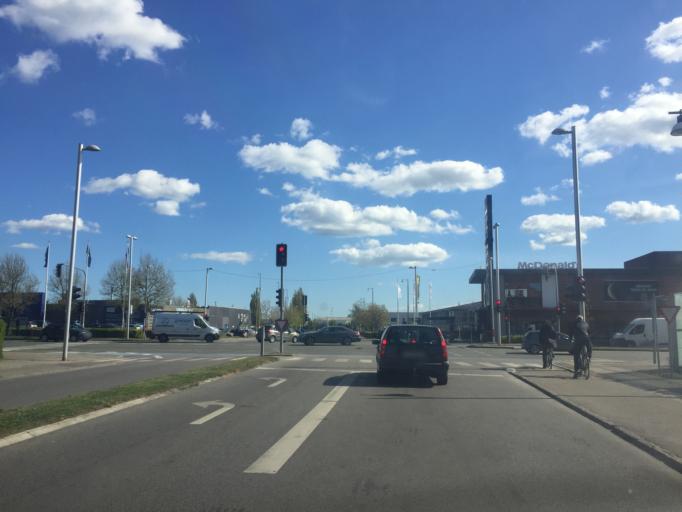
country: DK
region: Capital Region
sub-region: Albertslund Kommune
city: Albertslund
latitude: 55.6651
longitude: 12.3794
